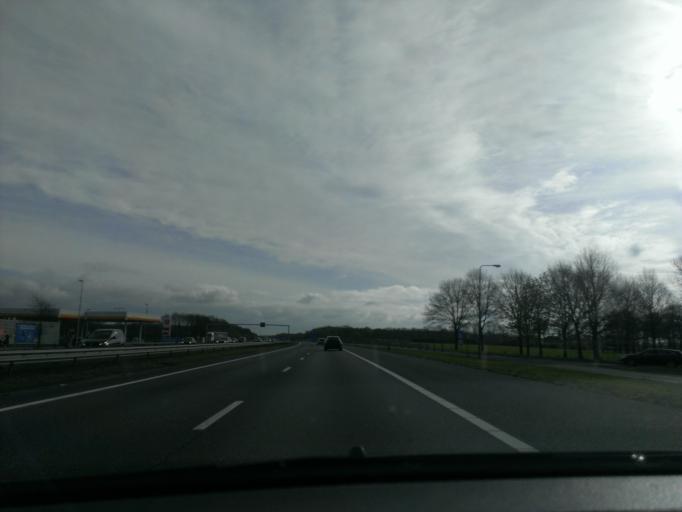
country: NL
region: Overijssel
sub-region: Gemeente Hof van Twente
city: Markelo
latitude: 52.2545
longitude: 6.4365
